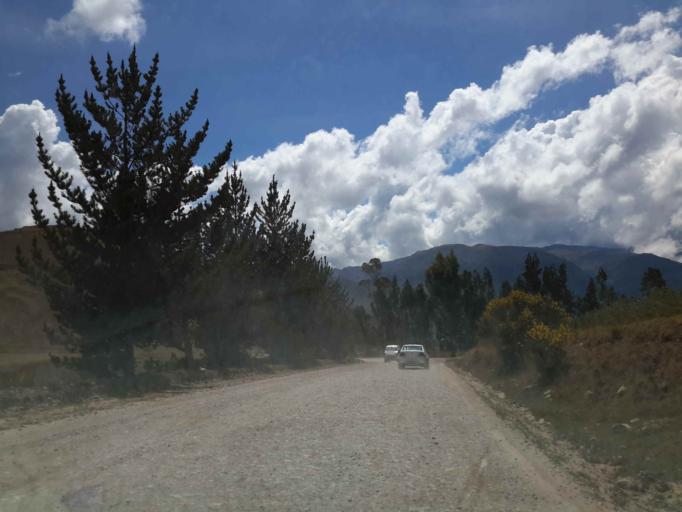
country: PE
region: Apurimac
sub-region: Provincia de Andahuaylas
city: Pacucha
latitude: -13.6305
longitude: -73.3386
